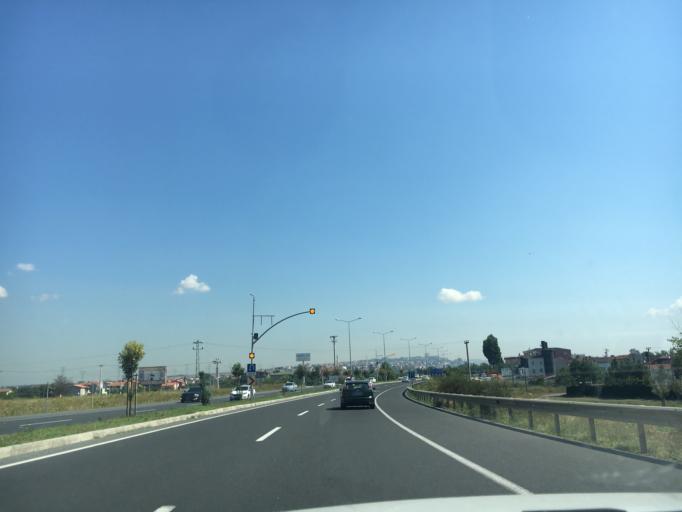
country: TR
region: Tekirdag
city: Sultankoy
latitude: 41.0059
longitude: 27.9779
